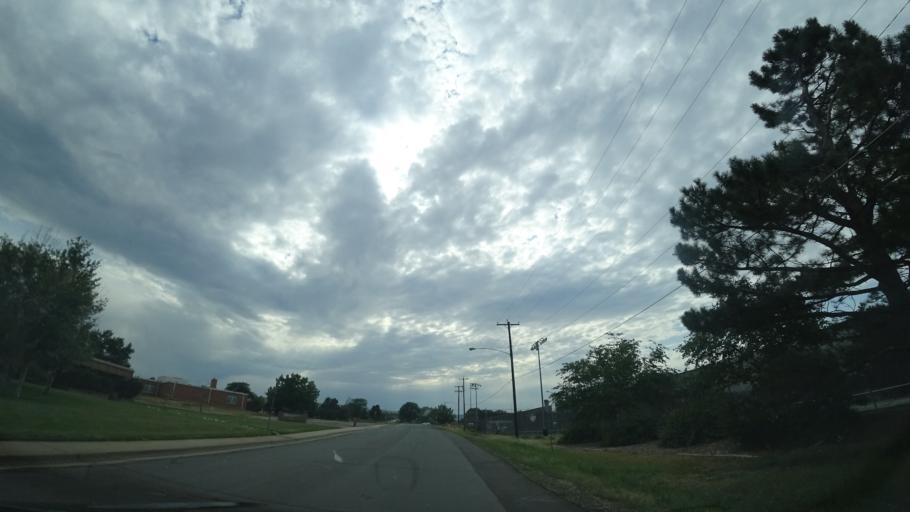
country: US
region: Colorado
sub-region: Jefferson County
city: Lakewood
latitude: 39.7130
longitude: -105.1069
